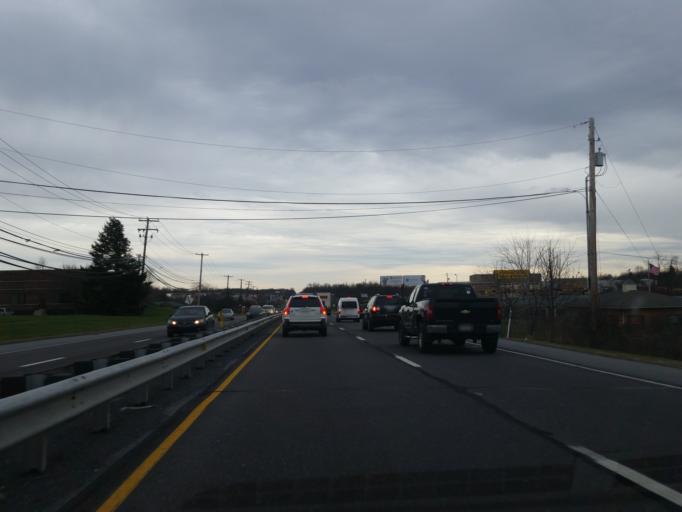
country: US
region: Pennsylvania
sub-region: Dauphin County
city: Linglestown
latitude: 40.3250
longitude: -76.7790
